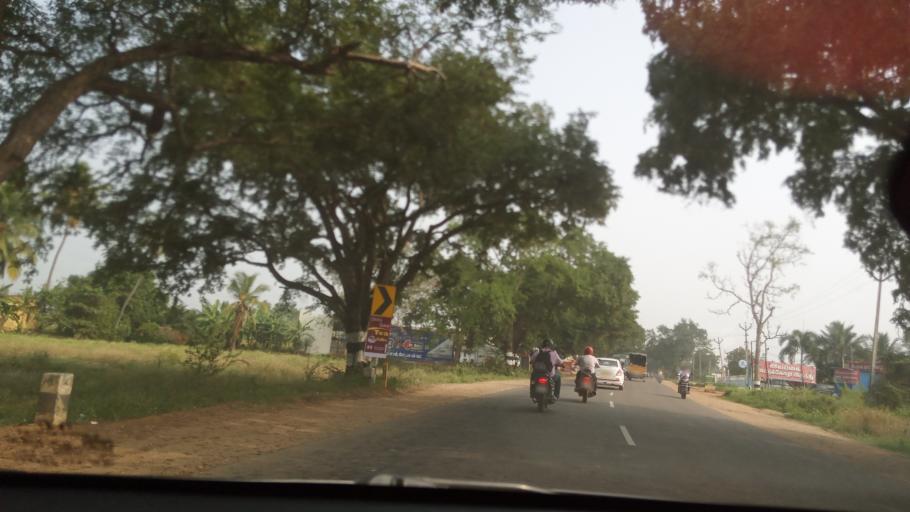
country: IN
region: Tamil Nadu
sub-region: Coimbatore
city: Annur
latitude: 11.1602
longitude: 77.0509
